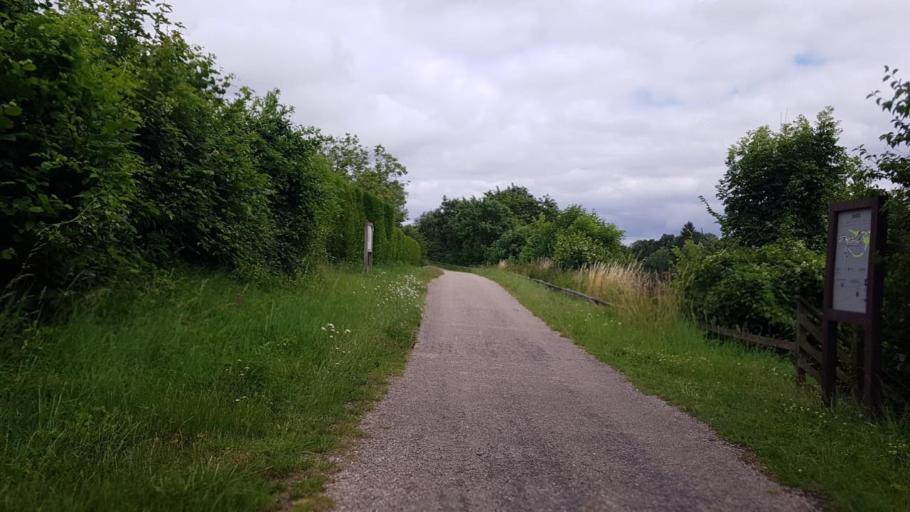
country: FR
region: Picardie
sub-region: Departement de l'Aisne
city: Origny-en-Thierache
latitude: 49.9320
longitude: 4.0104
